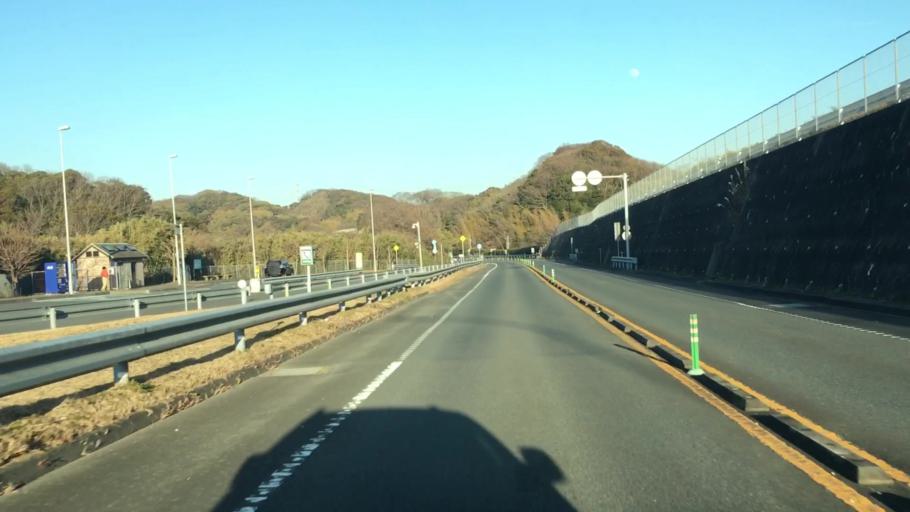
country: JP
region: Kanagawa
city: Yokosuka
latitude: 35.2275
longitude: 139.6408
